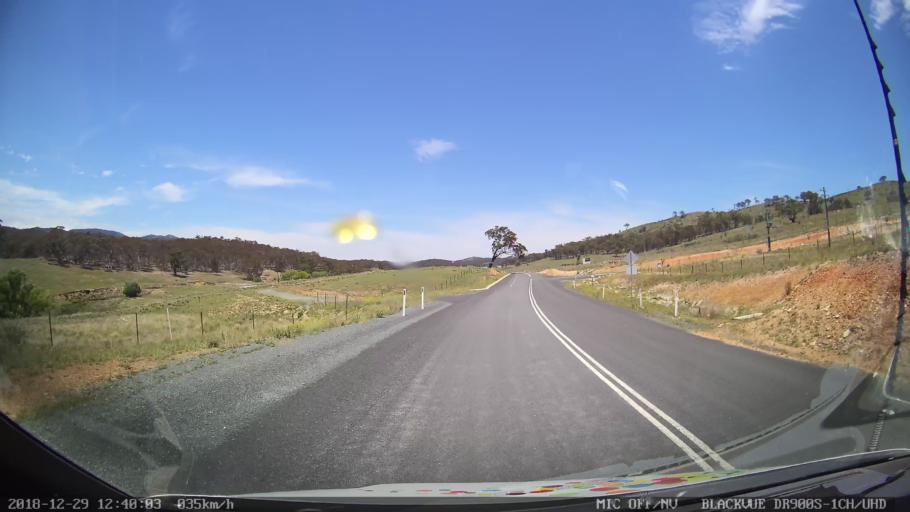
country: AU
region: Australian Capital Territory
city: Macarthur
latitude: -35.5987
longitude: 149.2262
